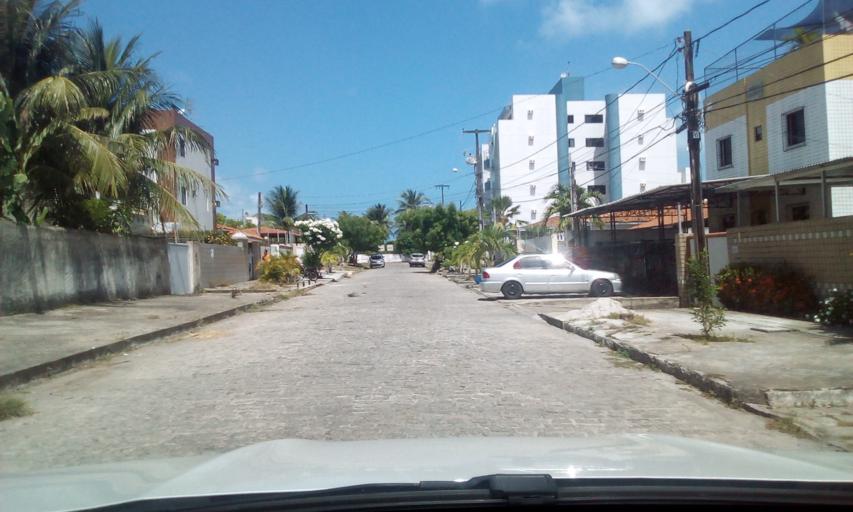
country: BR
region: Paraiba
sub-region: Joao Pessoa
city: Joao Pessoa
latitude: -7.0623
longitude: -34.8438
